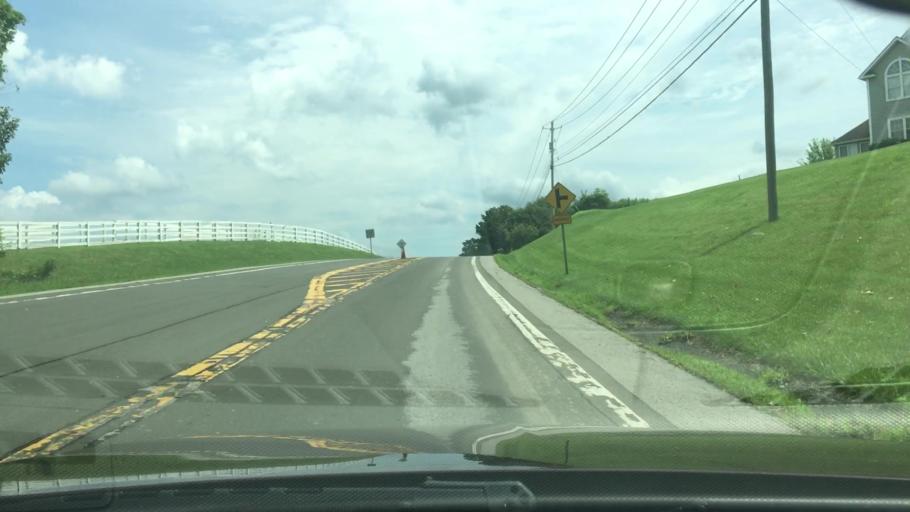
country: US
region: New York
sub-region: Dutchess County
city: Hillside Lake
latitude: 41.5914
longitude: -73.7005
